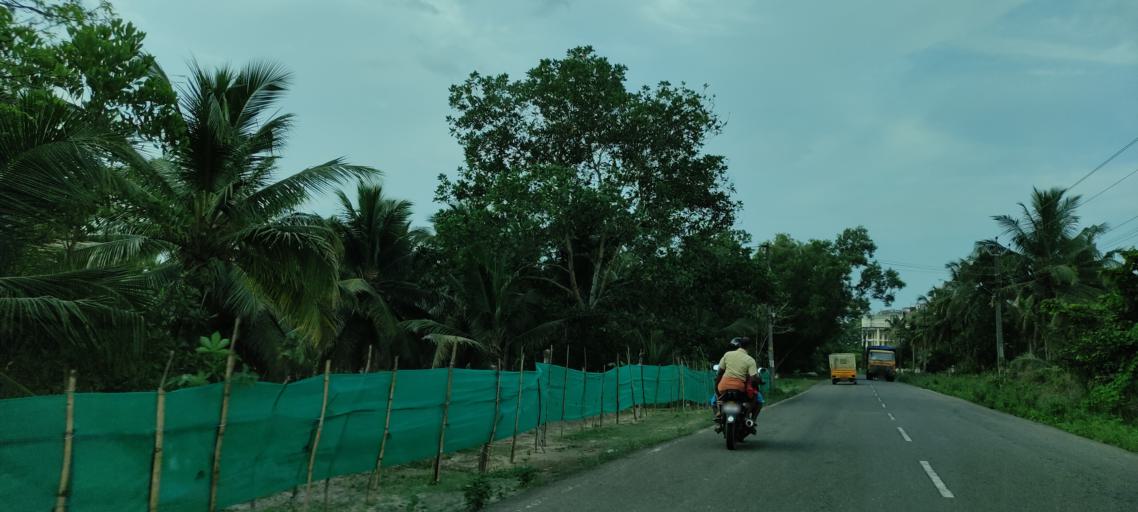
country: IN
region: Kerala
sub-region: Alappuzha
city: Kutiatodu
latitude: 9.7780
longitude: 76.3609
